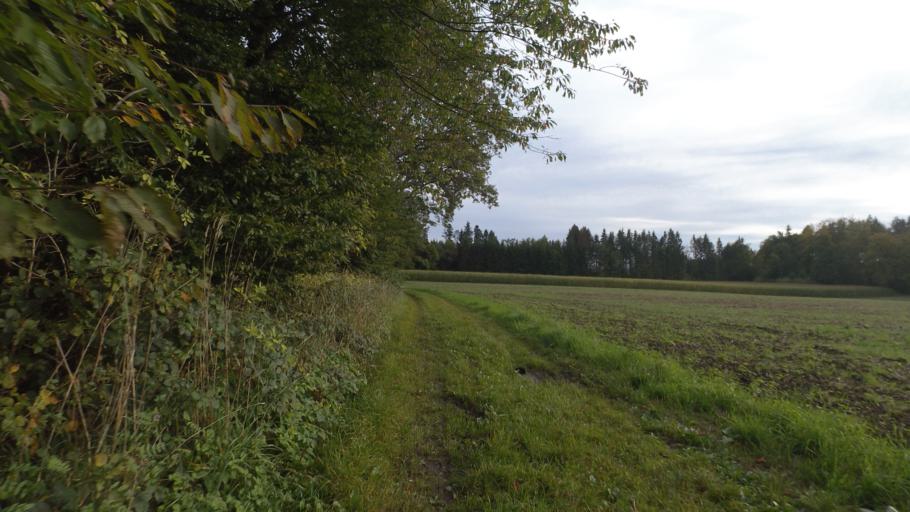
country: DE
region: Bavaria
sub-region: Upper Bavaria
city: Chieming
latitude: 47.9201
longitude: 12.5437
